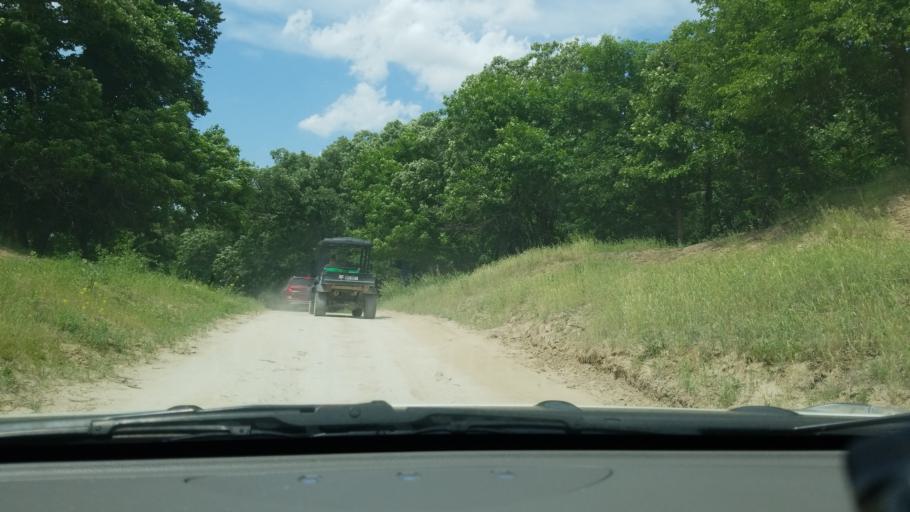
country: US
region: Nebraska
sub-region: Saunders County
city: Ashland
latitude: 41.0168
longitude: -96.2919
